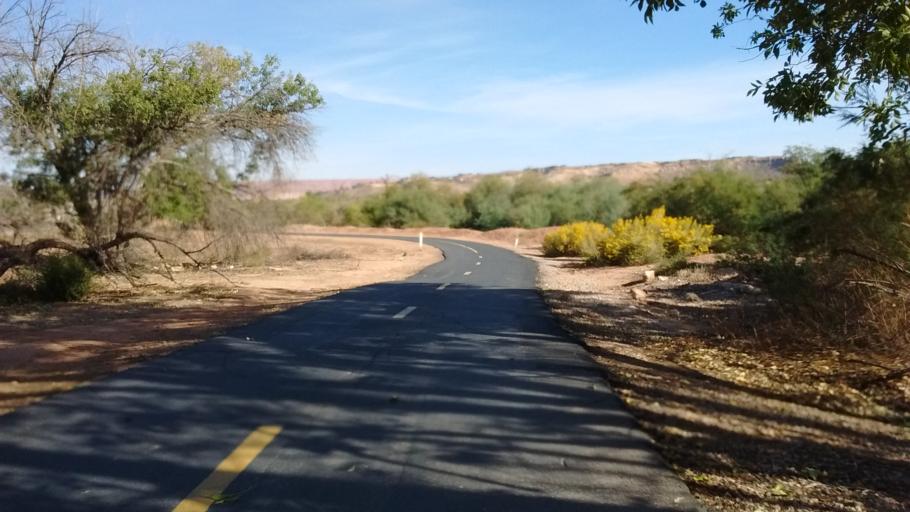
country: US
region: Utah
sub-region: Washington County
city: Saint George
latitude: 37.0867
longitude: -113.5684
